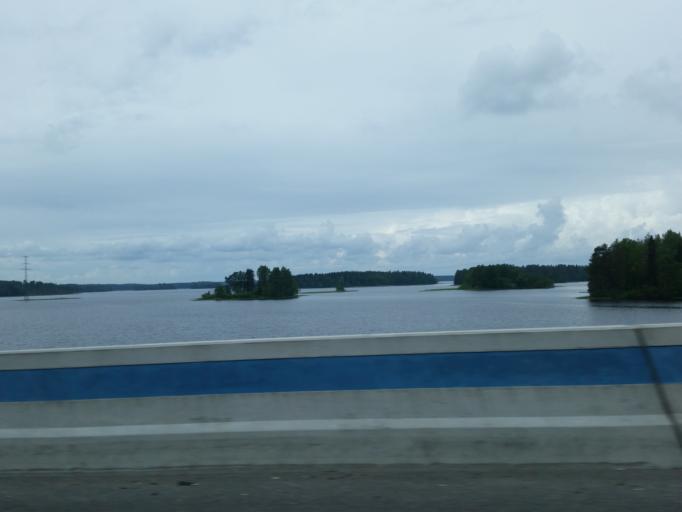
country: FI
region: Northern Savo
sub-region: Kuopio
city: Kuopio
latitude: 62.9447
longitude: 27.6692
